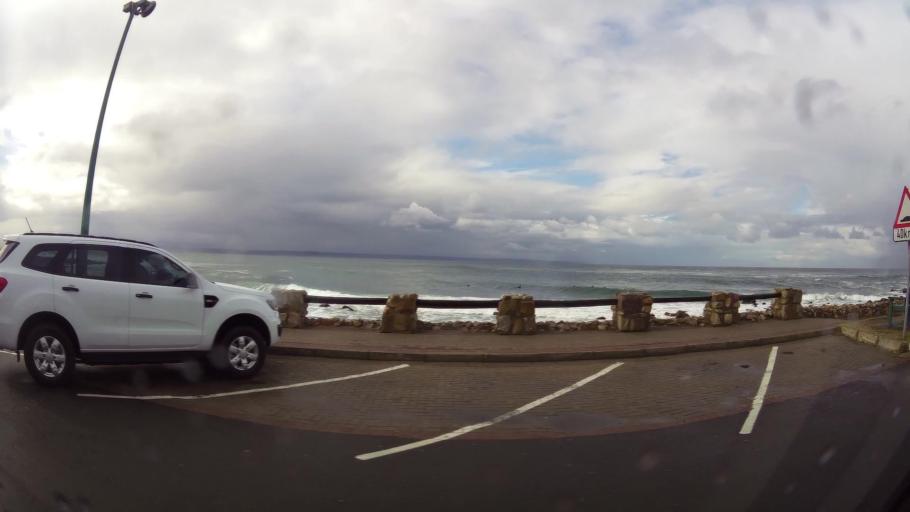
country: ZA
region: Western Cape
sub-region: Eden District Municipality
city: Mossel Bay
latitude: -34.1845
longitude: 22.1587
